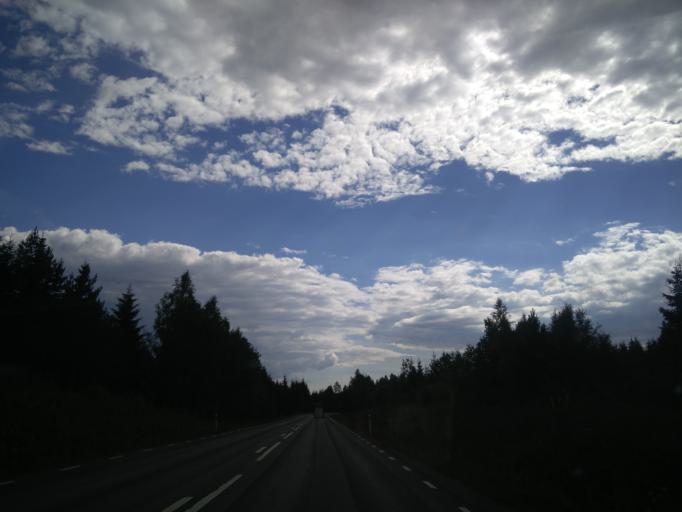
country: SE
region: Vaermland
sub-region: Filipstads Kommun
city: Filipstad
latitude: 59.7814
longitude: 14.3002
